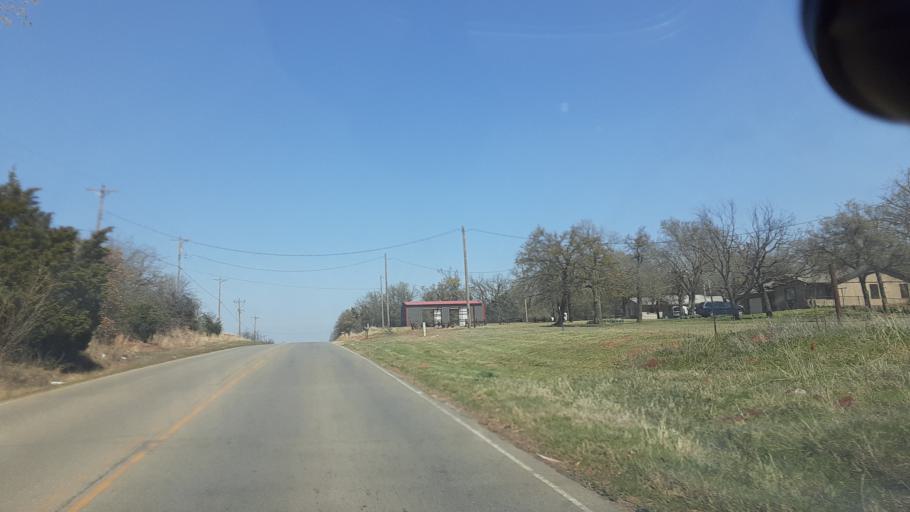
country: US
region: Oklahoma
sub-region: Oklahoma County
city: Edmond
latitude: 35.7480
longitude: -97.4783
